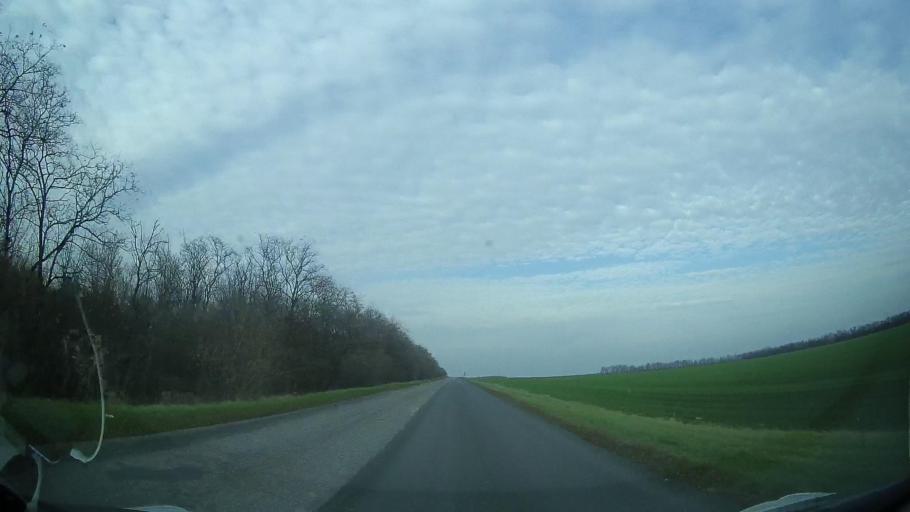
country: RU
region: Rostov
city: Zernograd
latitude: 46.9593
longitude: 40.3668
